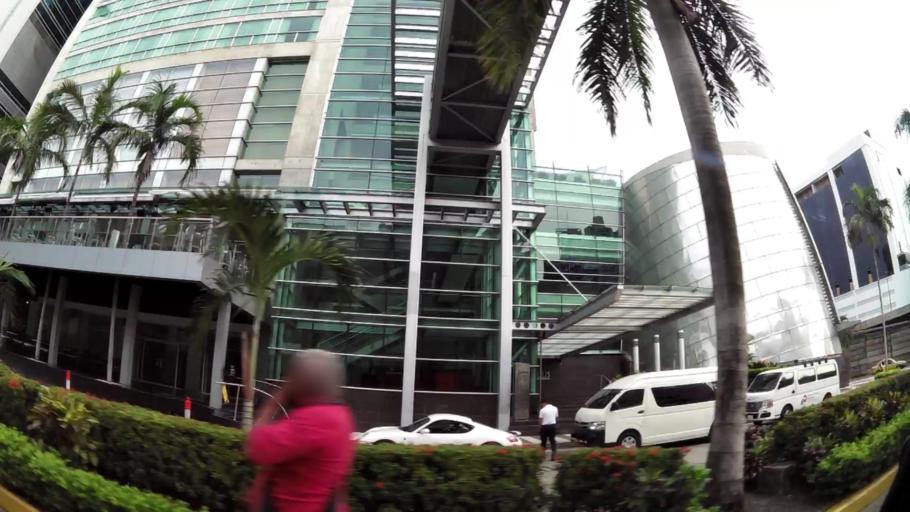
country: PA
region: Panama
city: Panama
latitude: 8.9773
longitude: -79.5169
